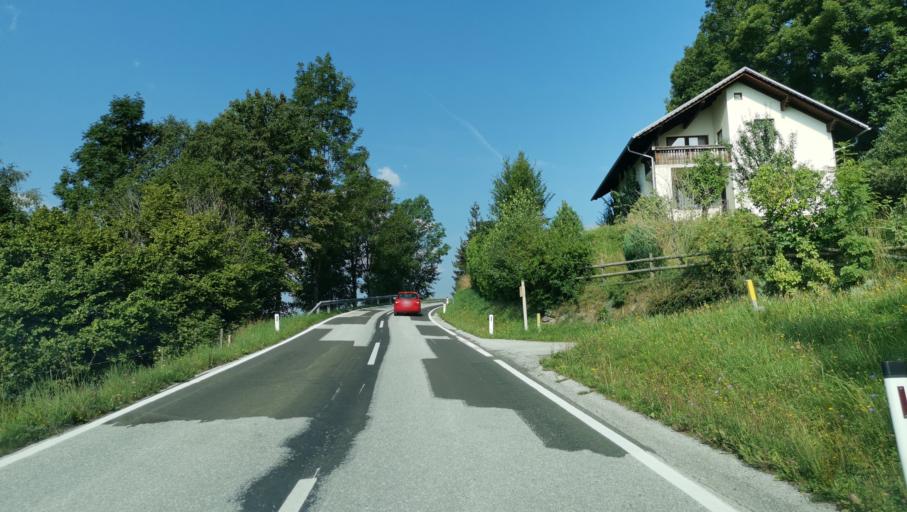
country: AT
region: Styria
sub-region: Politischer Bezirk Liezen
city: Trieben
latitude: 47.5154
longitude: 14.4504
